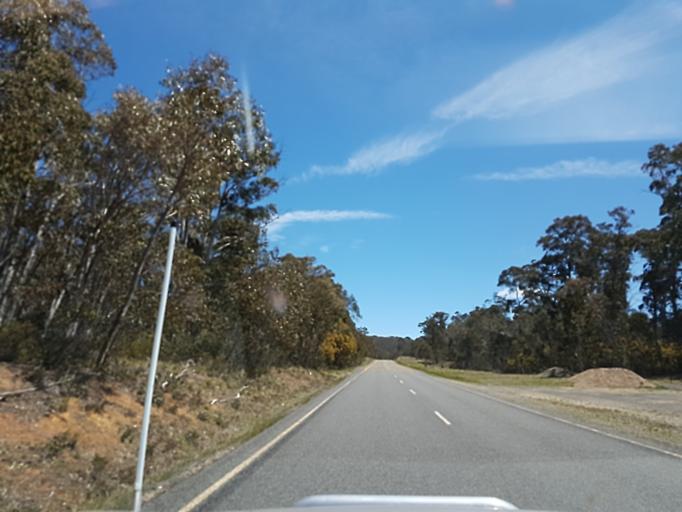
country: AU
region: Victoria
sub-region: Alpine
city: Mount Beauty
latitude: -37.0664
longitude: 147.3408
